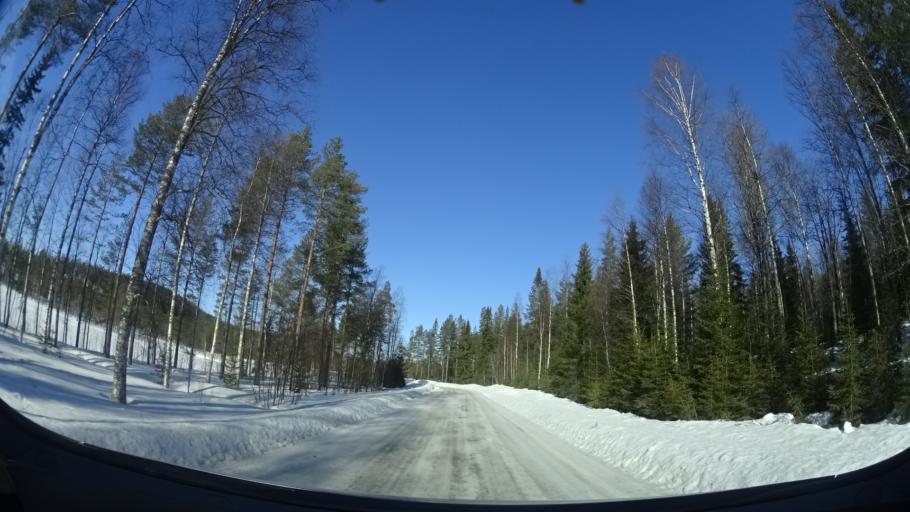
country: SE
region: Vaesterbotten
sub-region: Skelleftea Kommun
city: Langsele
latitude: 65.1625
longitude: 20.1510
